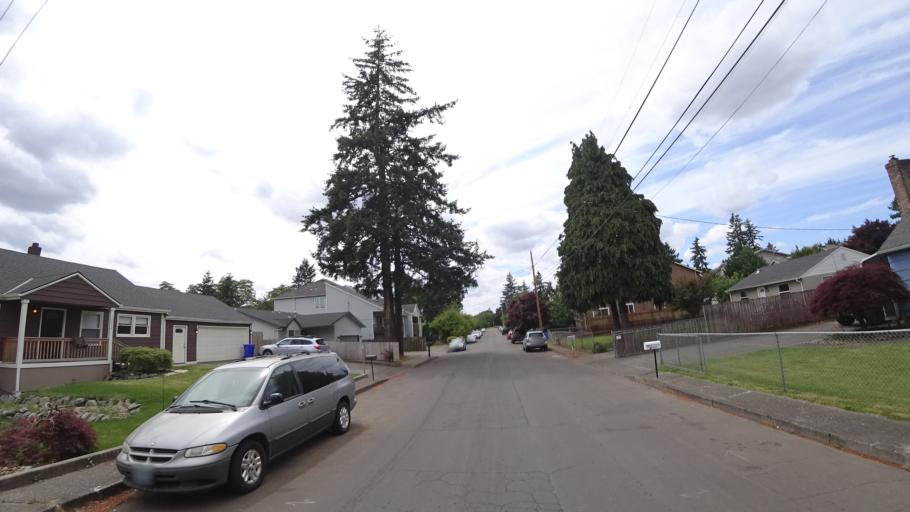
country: US
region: Oregon
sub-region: Multnomah County
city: Lents
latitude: 45.4868
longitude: -122.5393
